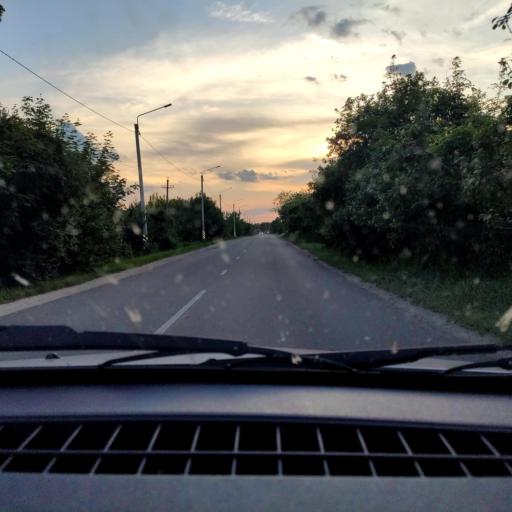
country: RU
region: Voronezj
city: Ramon'
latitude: 51.9519
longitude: 39.3651
